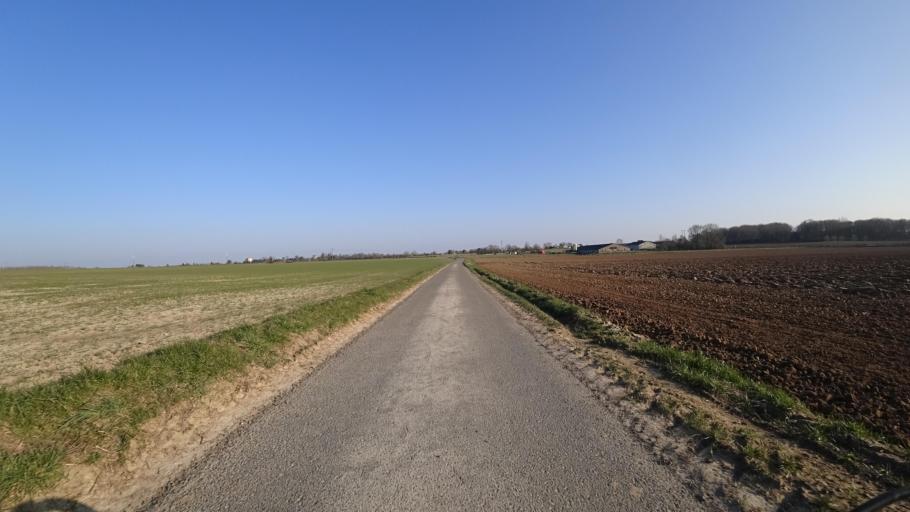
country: BE
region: Wallonia
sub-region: Province de Namur
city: Gembloux
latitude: 50.5709
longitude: 4.6664
